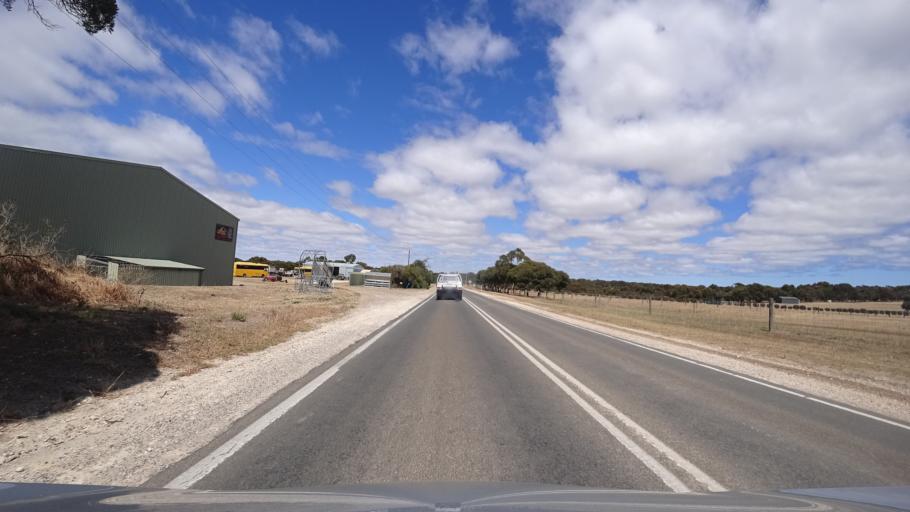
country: AU
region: South Australia
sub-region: Kangaroo Island
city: Kingscote
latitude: -35.6547
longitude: 137.6207
